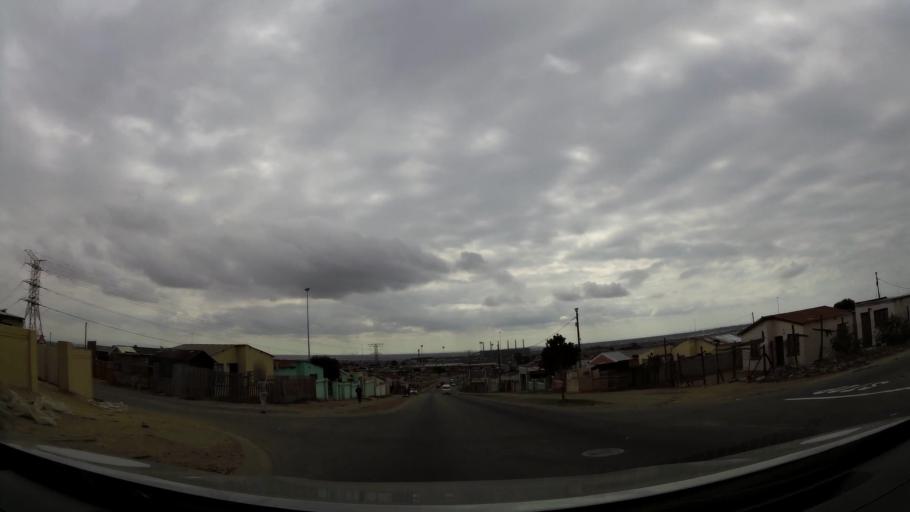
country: ZA
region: Eastern Cape
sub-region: Nelson Mandela Bay Metropolitan Municipality
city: Port Elizabeth
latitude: -33.8905
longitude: 25.5952
